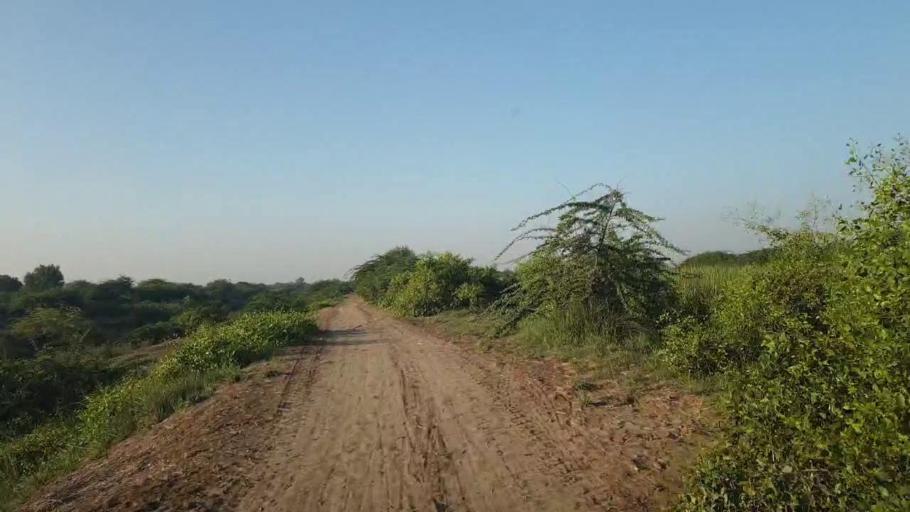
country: PK
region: Sindh
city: Badin
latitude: 24.6259
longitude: 68.7944
